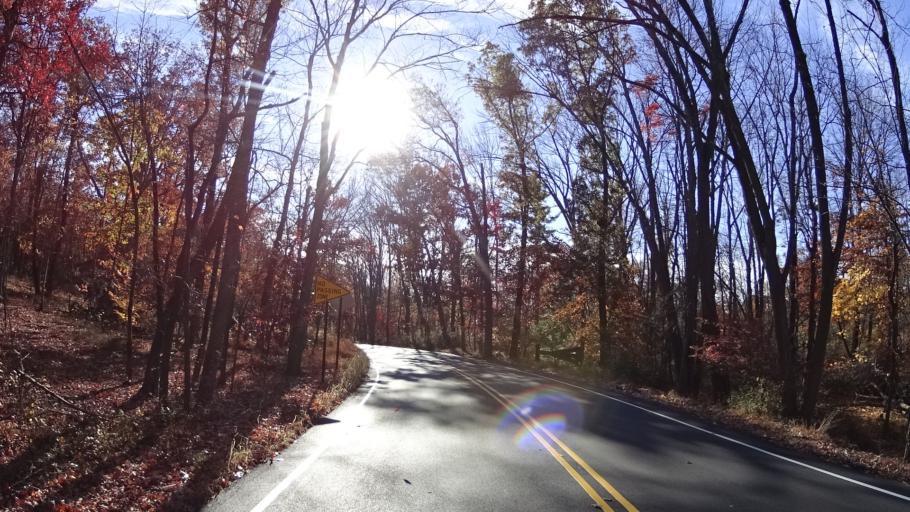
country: US
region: New Jersey
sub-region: Union County
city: Scotch Plains
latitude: 40.6731
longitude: -74.3886
